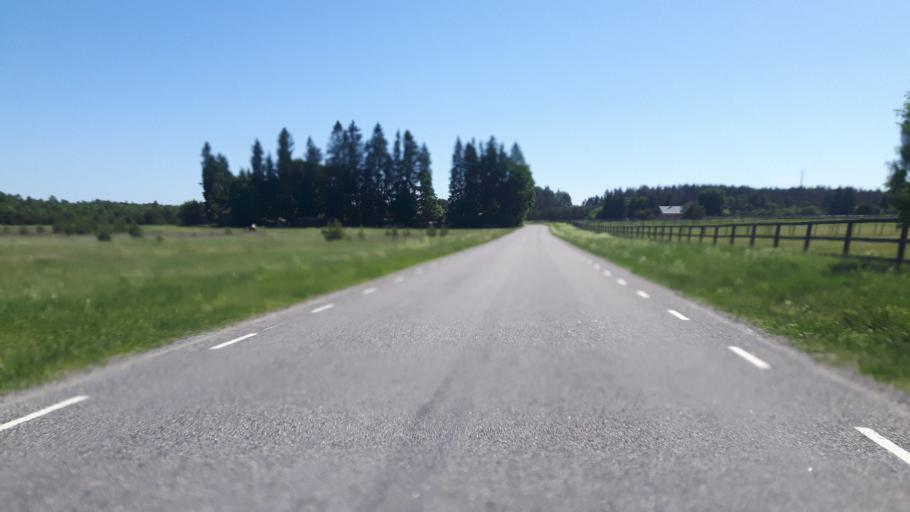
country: EE
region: Raplamaa
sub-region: Kohila vald
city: Kohila
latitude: 59.1968
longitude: 24.6972
